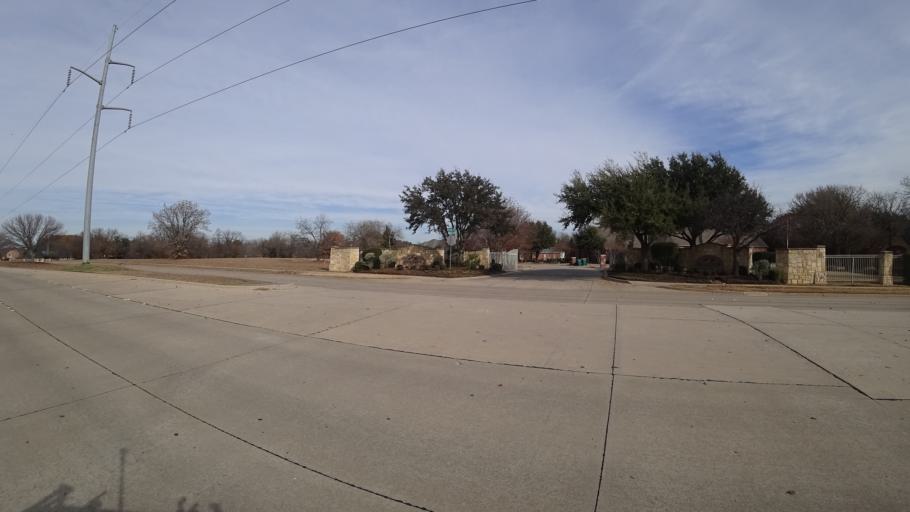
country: US
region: Texas
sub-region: Denton County
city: Highland Village
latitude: 33.0783
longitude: -97.0378
